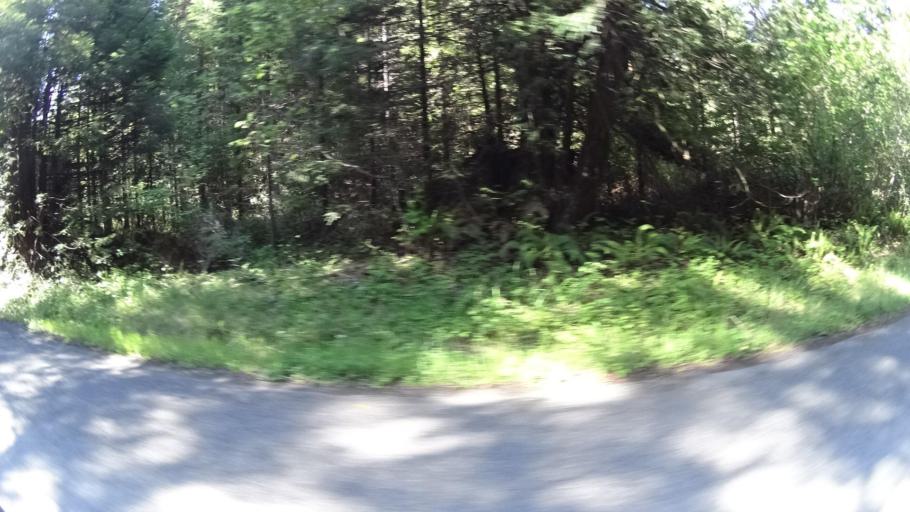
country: US
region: California
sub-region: Humboldt County
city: Rio Dell
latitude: 40.4374
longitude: -123.9677
